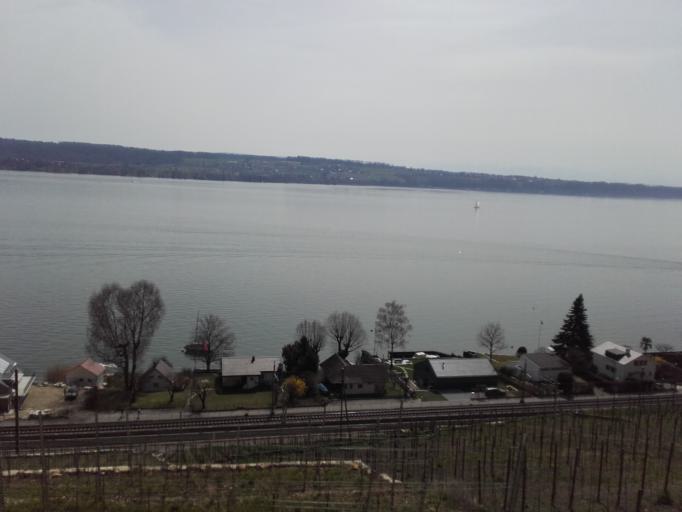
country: CH
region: Bern
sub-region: Seeland District
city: Tauffelen
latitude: 47.1079
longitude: 7.1807
